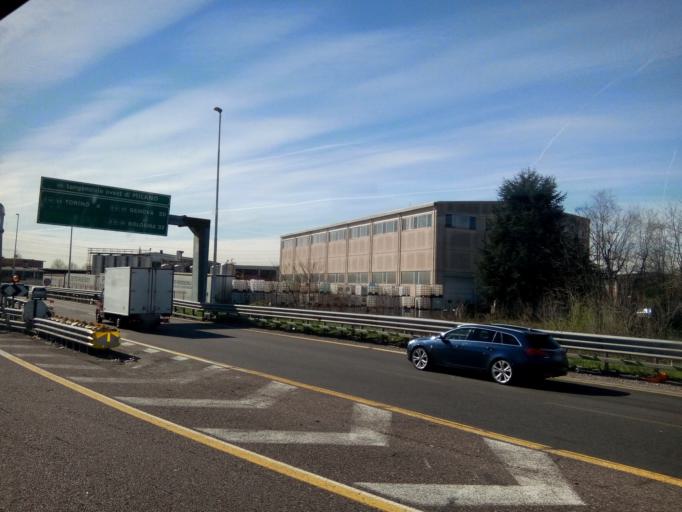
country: IT
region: Lombardy
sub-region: Citta metropolitana di Milano
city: Passirana
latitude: 45.5496
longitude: 9.0573
